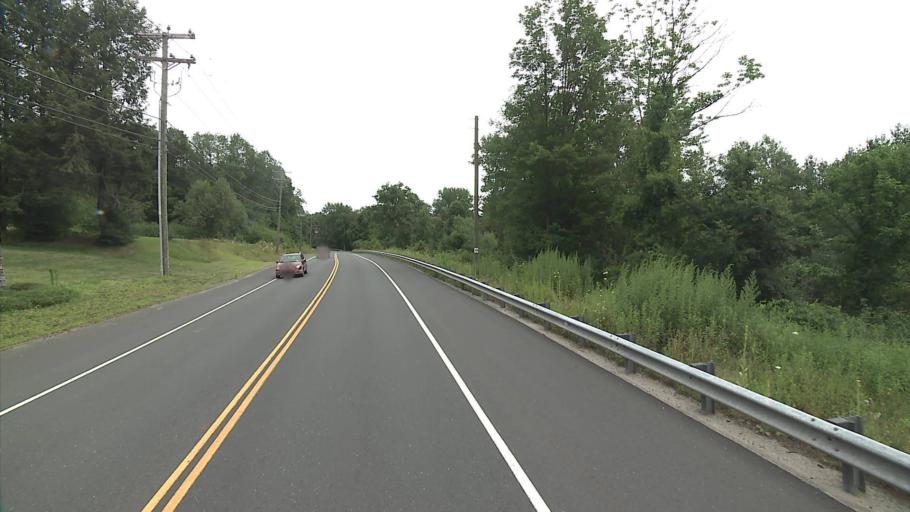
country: US
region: Connecticut
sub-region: Litchfield County
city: Winsted
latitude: 41.9532
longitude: -73.0484
